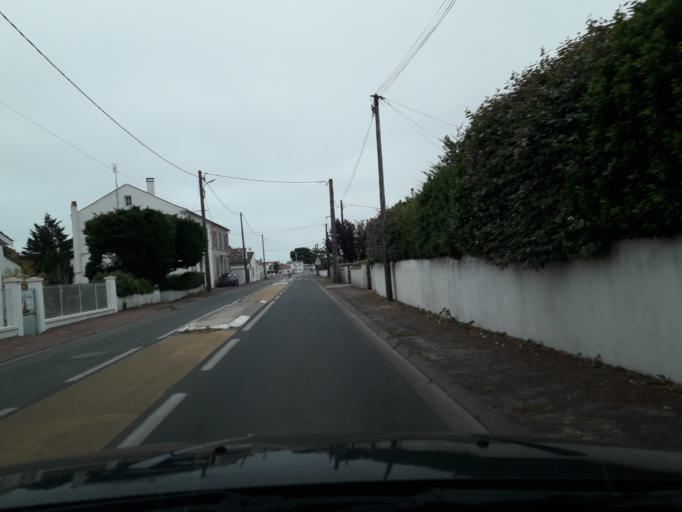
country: FR
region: Poitou-Charentes
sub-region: Departement de la Charente-Maritime
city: Boyard-Ville
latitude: 45.9656
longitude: -1.2460
